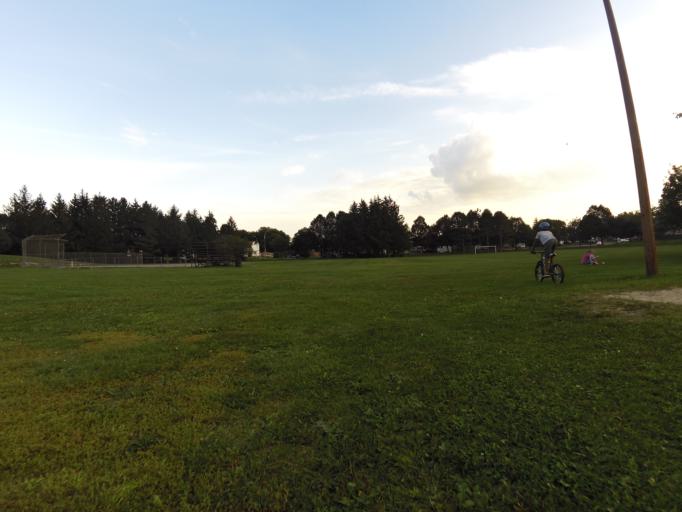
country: CA
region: Ontario
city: Bells Corners
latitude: 45.2734
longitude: -75.7520
